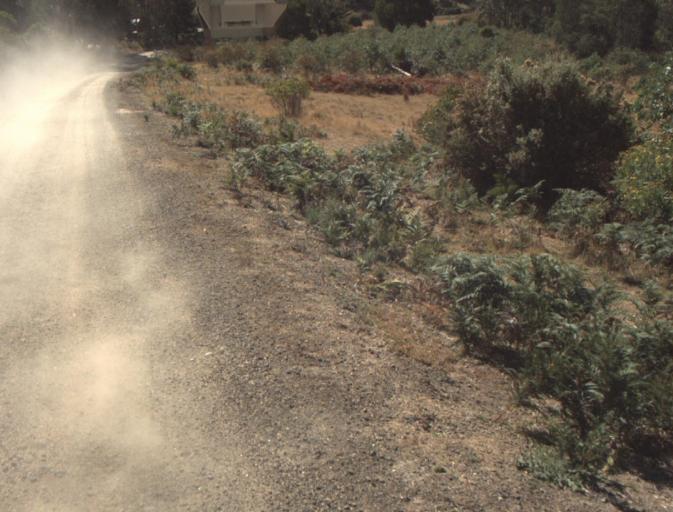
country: AU
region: Tasmania
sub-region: Dorset
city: Scottsdale
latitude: -41.3164
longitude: 147.3819
